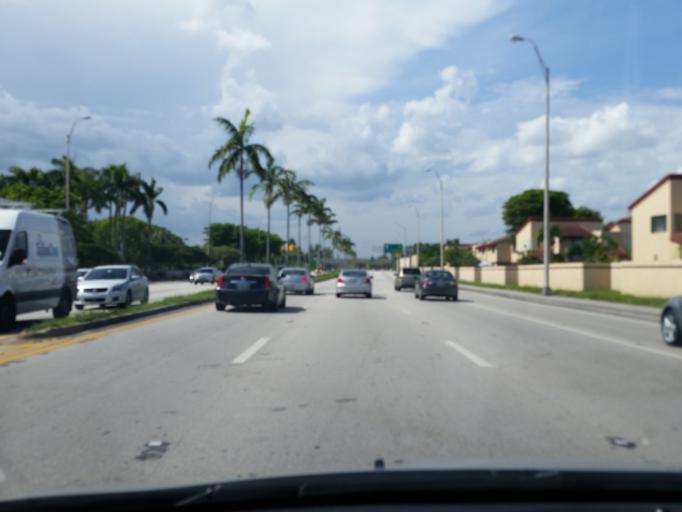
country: US
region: Florida
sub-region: Miami-Dade County
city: Sweetwater
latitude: 25.7757
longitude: -80.3696
